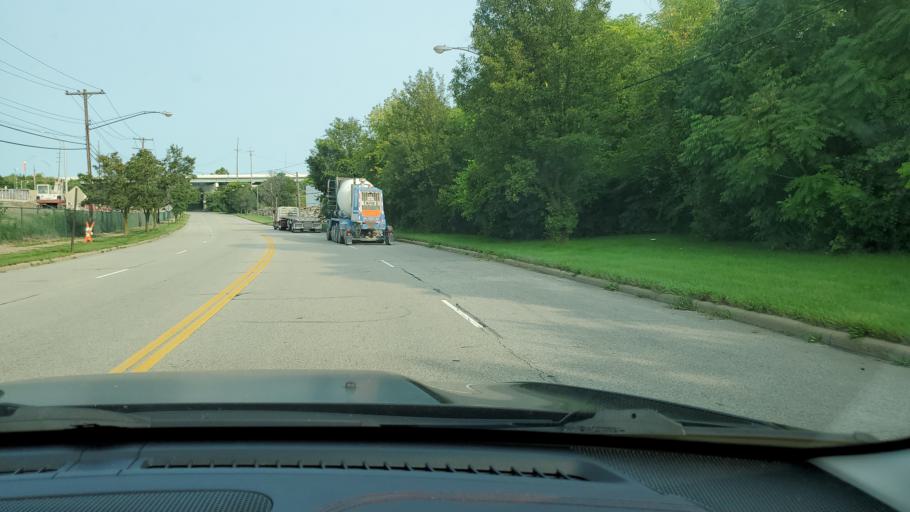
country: US
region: Ohio
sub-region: Mahoning County
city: Youngstown
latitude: 41.0899
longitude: -80.6401
